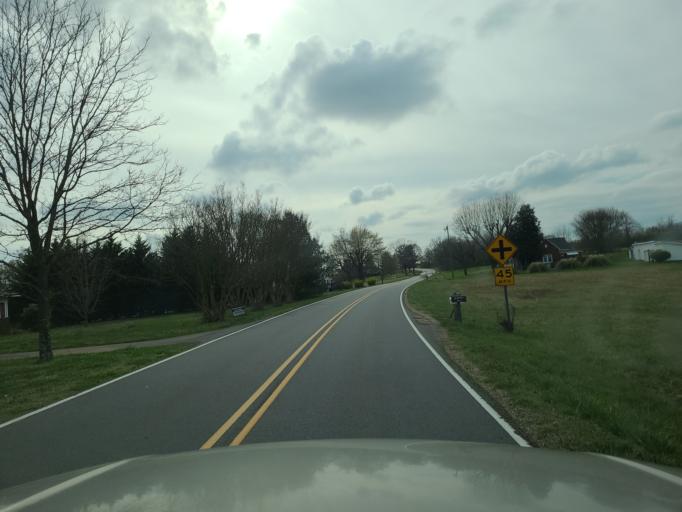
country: US
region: North Carolina
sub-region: Cleveland County
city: Boiling Springs
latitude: 35.2441
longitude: -81.7286
